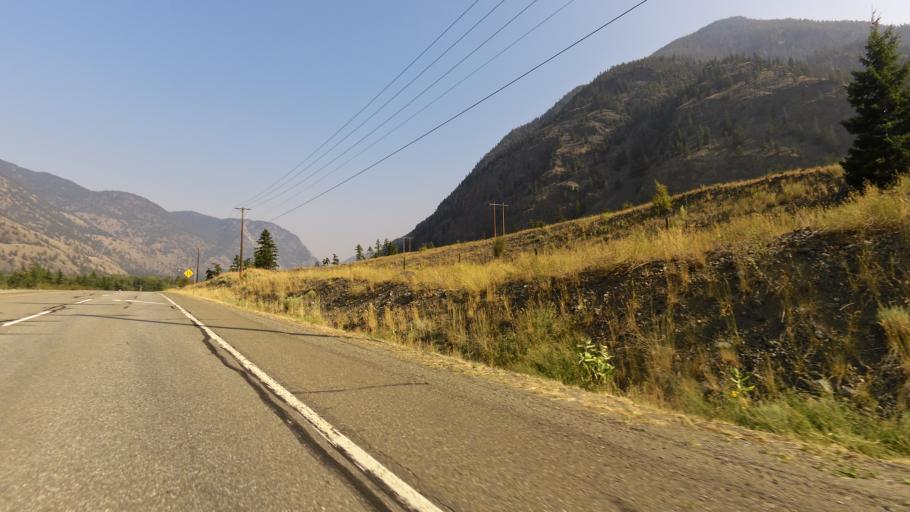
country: CA
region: British Columbia
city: Oliver
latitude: 49.2507
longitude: -120.0090
